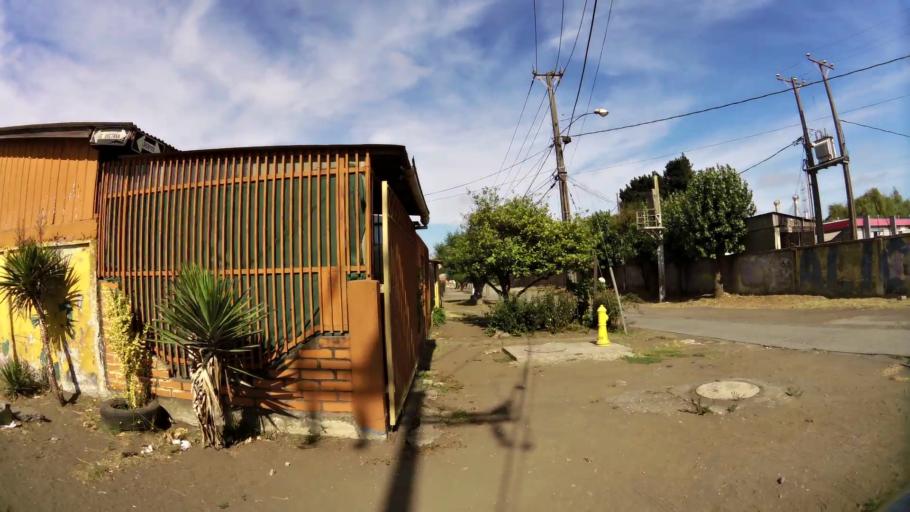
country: CL
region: Biobio
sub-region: Provincia de Concepcion
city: Talcahuano
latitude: -36.7773
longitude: -73.1132
